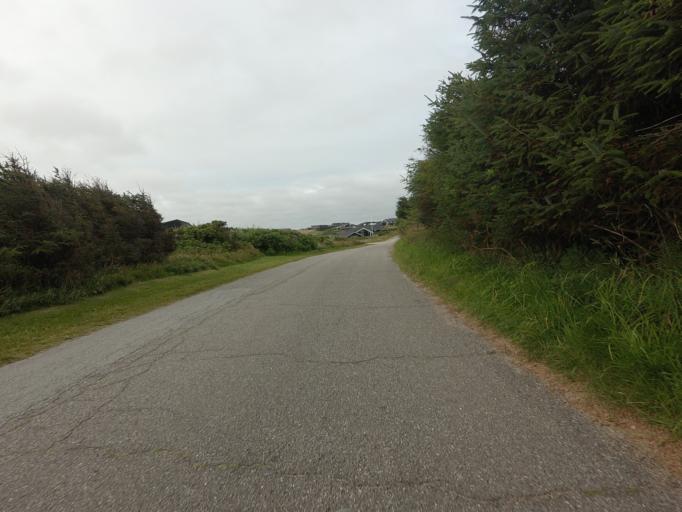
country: DK
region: North Denmark
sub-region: Jammerbugt Kommune
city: Pandrup
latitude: 57.3886
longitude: 9.7284
